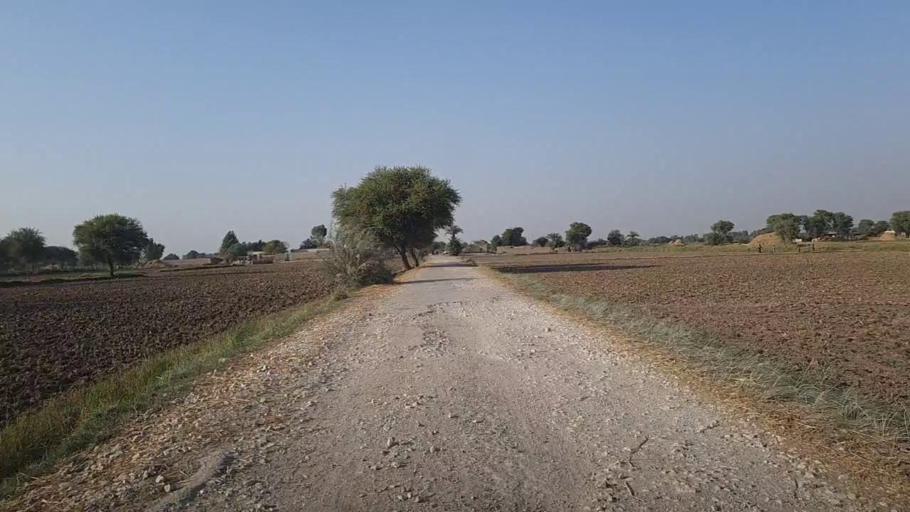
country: PK
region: Sindh
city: Kashmor
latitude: 28.4113
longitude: 69.4119
